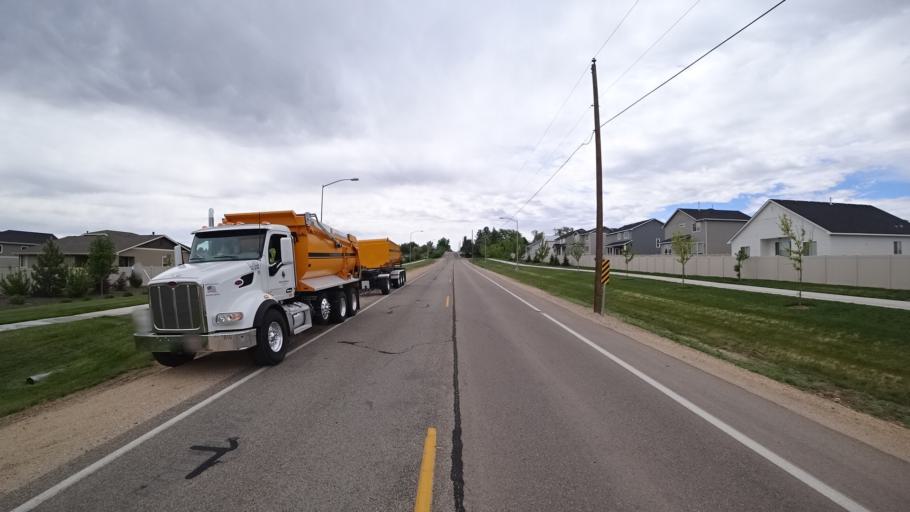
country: US
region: Idaho
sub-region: Ada County
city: Meridian
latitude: 43.5844
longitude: -116.4137
